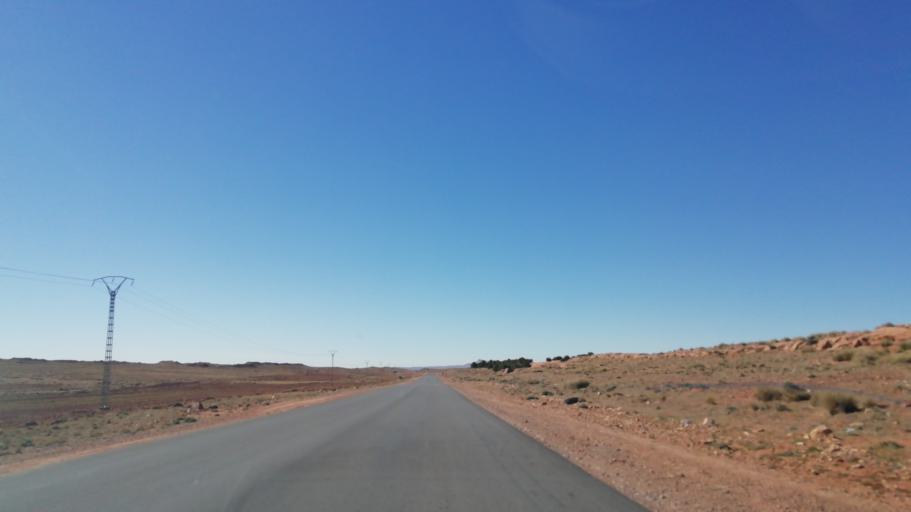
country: DZ
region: El Bayadh
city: El Bayadh
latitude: 33.6492
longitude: 1.4038
